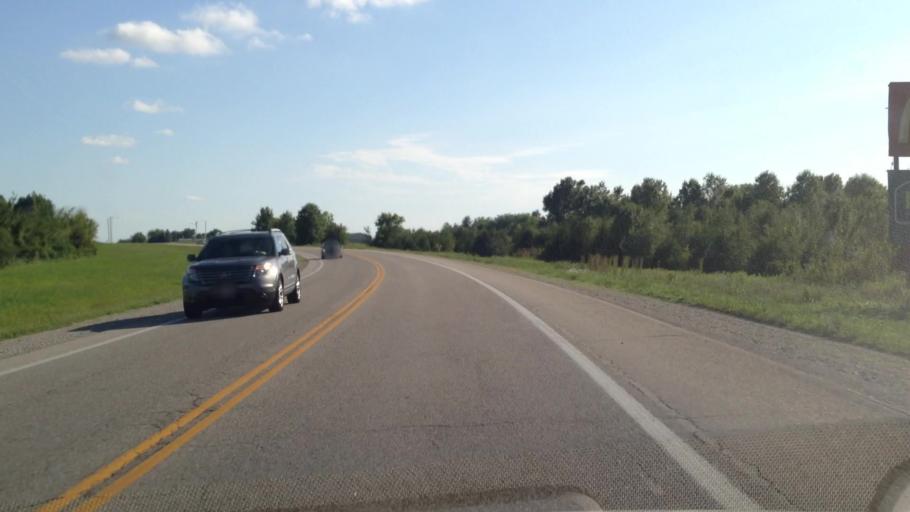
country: US
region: Kansas
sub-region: Crawford County
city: Arma
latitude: 37.5502
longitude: -94.7098
